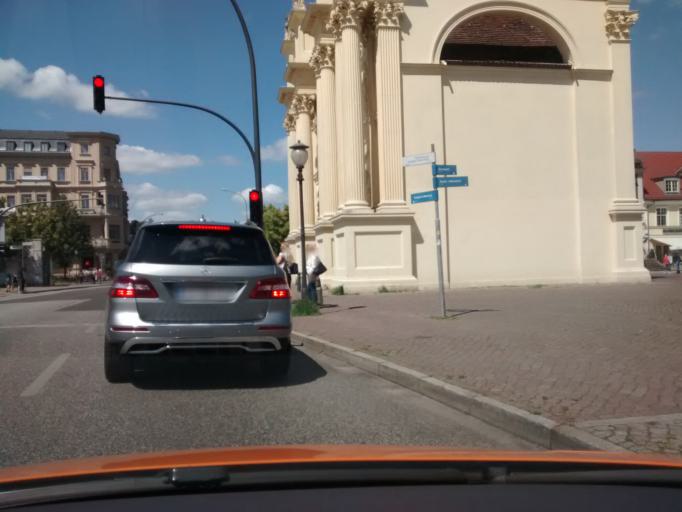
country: DE
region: Brandenburg
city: Potsdam
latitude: 52.3993
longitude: 13.0480
